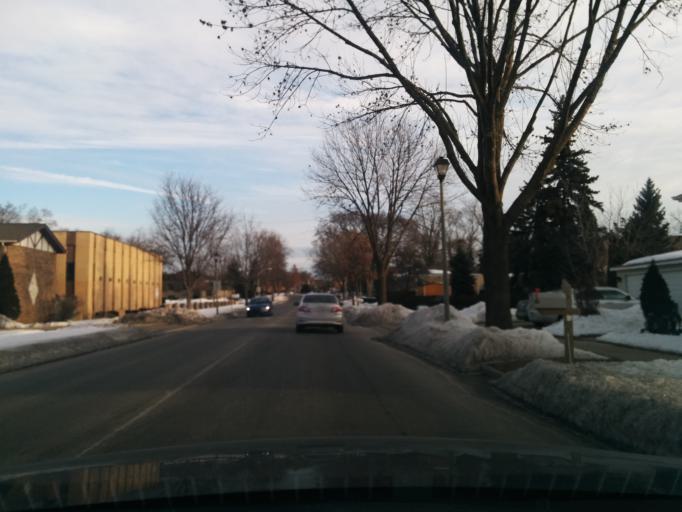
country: US
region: Illinois
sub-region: DuPage County
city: Elmhurst
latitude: 41.9029
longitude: -87.9592
